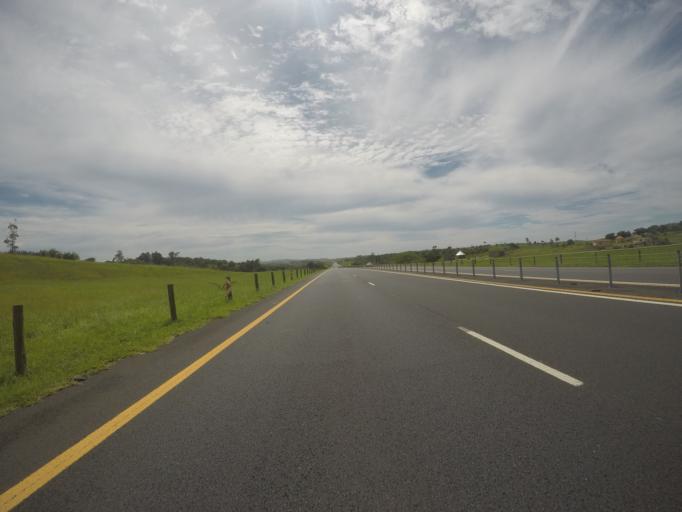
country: ZA
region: KwaZulu-Natal
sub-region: iLembe District Municipality
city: Mandeni
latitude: -29.1836
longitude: 31.4851
